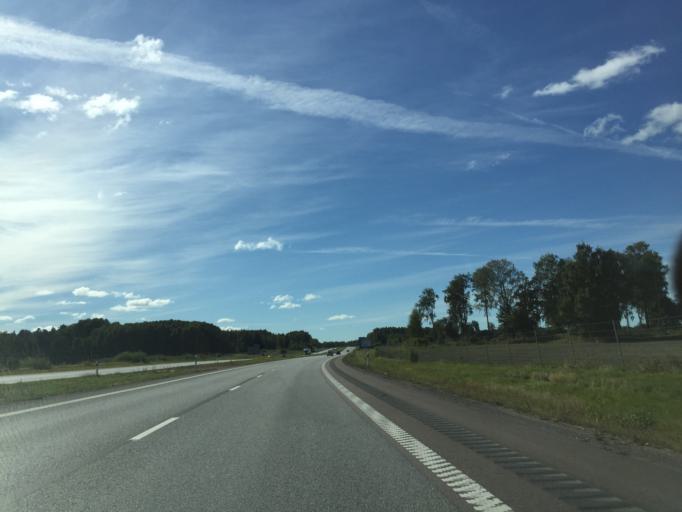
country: SE
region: Vaestmanland
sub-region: Kopings Kommun
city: Koping
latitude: 59.5183
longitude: 15.9638
